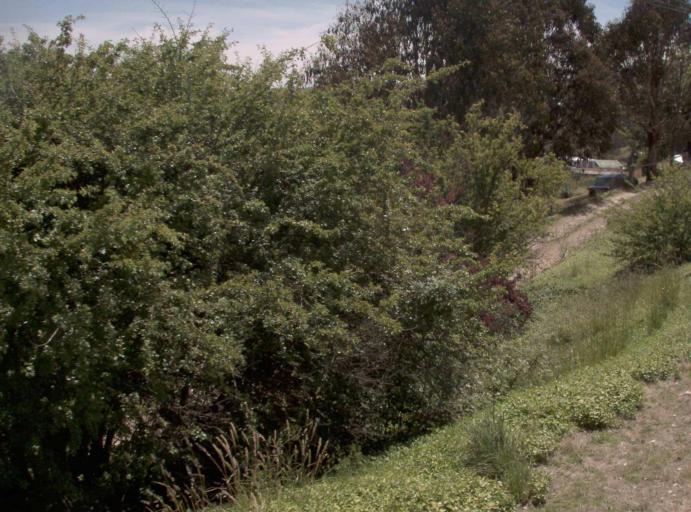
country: AU
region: Victoria
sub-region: Alpine
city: Mount Beauty
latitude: -37.1024
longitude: 147.5880
